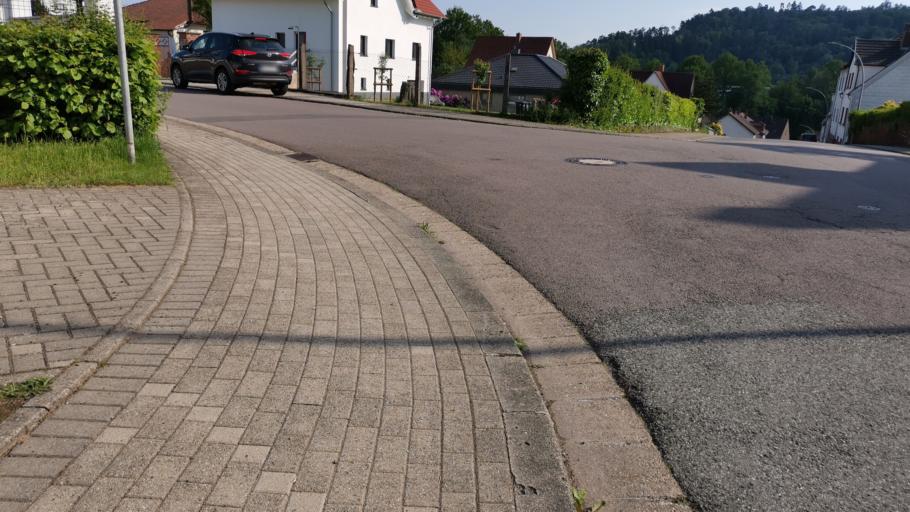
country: DE
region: Saarland
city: Sankt Ingbert
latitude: 49.2786
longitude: 7.1628
